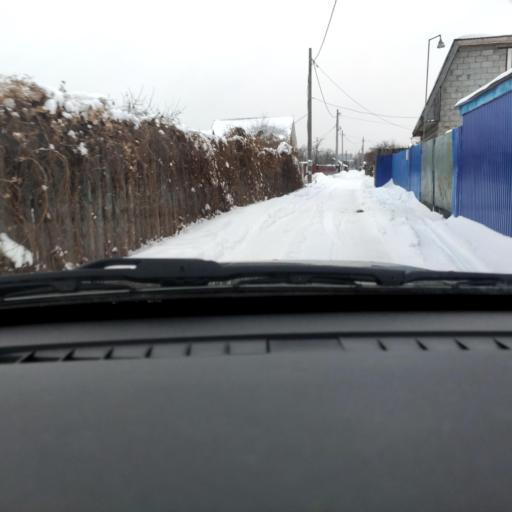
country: RU
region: Samara
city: Tol'yatti
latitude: 53.5417
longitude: 49.4351
